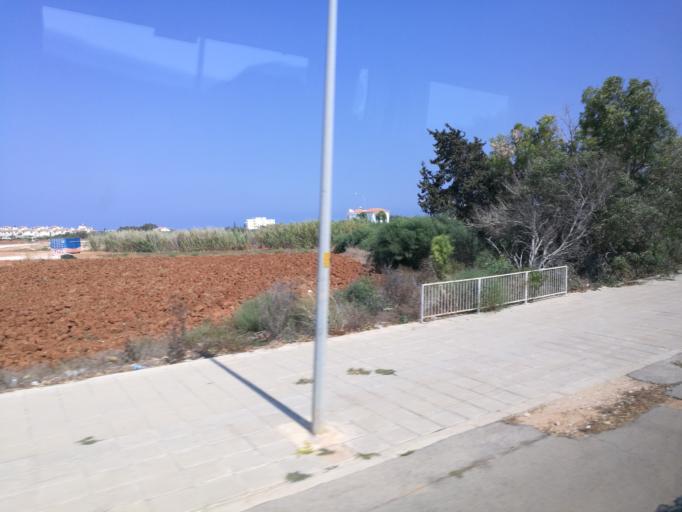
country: CY
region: Ammochostos
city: Protaras
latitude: 35.0296
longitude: 34.0297
